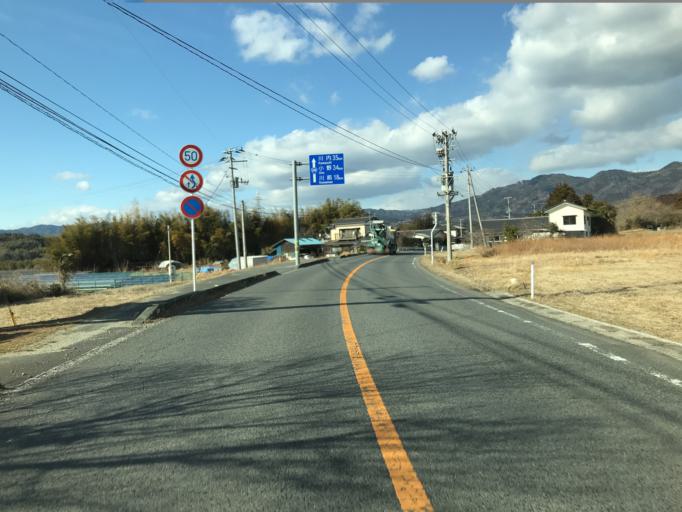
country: JP
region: Fukushima
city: Iwaki
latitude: 37.1143
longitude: 140.8709
